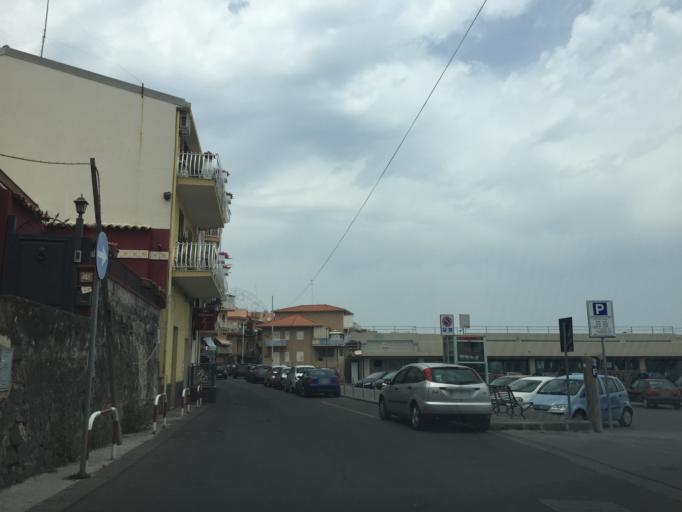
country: IT
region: Sicily
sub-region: Catania
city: Aci Trezza
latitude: 37.5639
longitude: 15.1623
